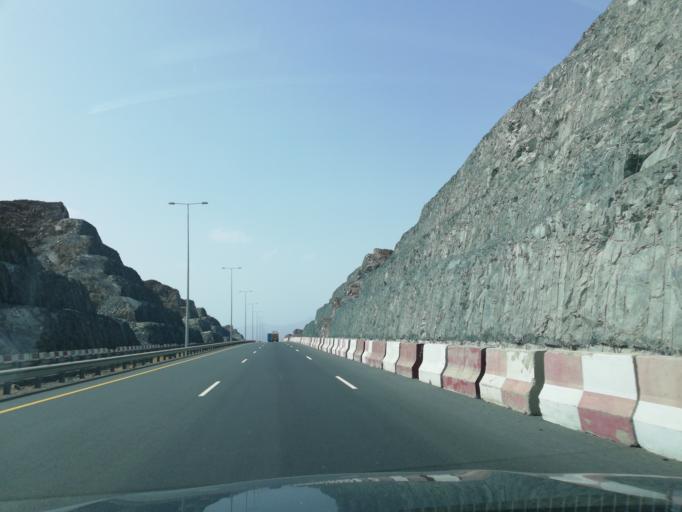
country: OM
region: Muhafazat ad Dakhiliyah
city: Sufalat Sama'il
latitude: 22.9924
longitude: 58.2314
